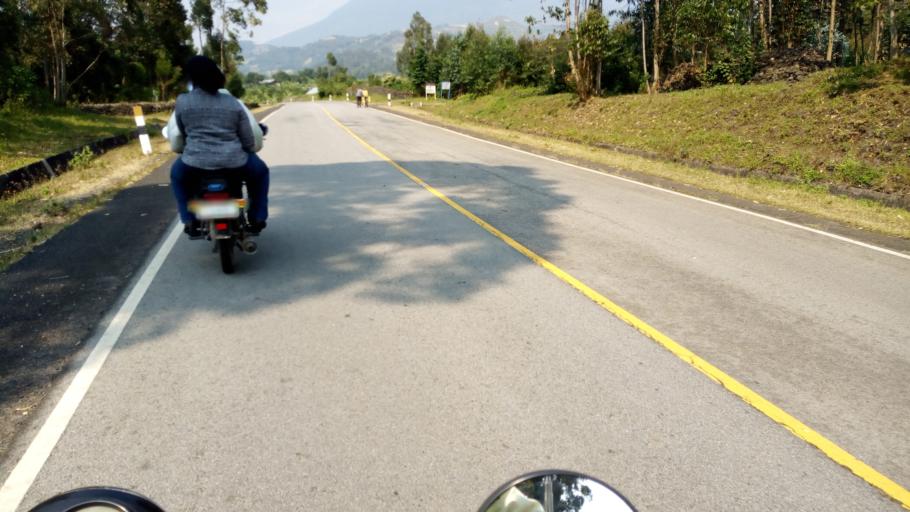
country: UG
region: Western Region
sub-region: Kisoro District
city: Kisoro
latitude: -1.3261
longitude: 29.7292
